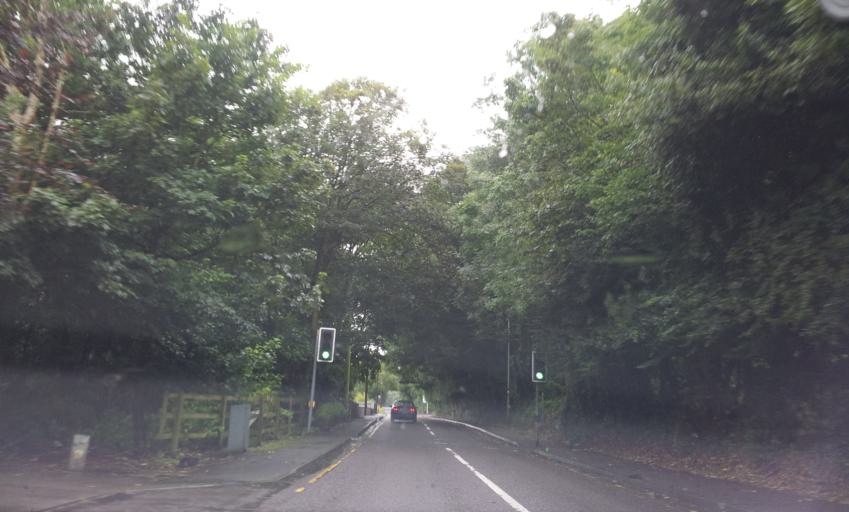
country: IE
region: Munster
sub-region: County Cork
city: Tower
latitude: 51.9280
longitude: -8.5977
